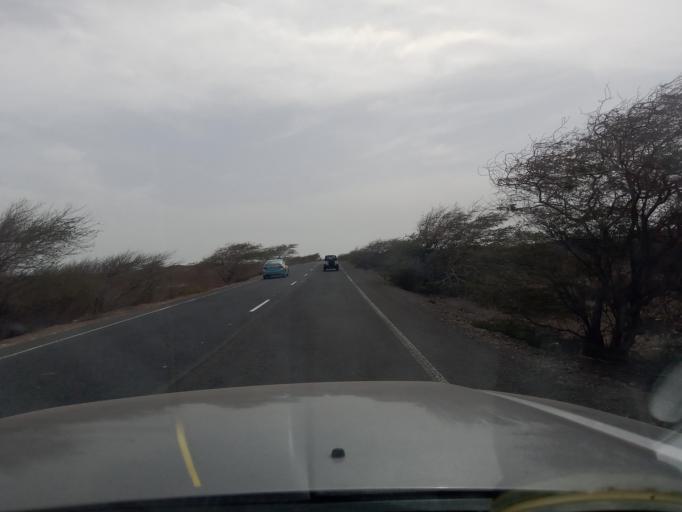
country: CV
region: Sal
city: Santa Maria
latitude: 16.6580
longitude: -22.9252
